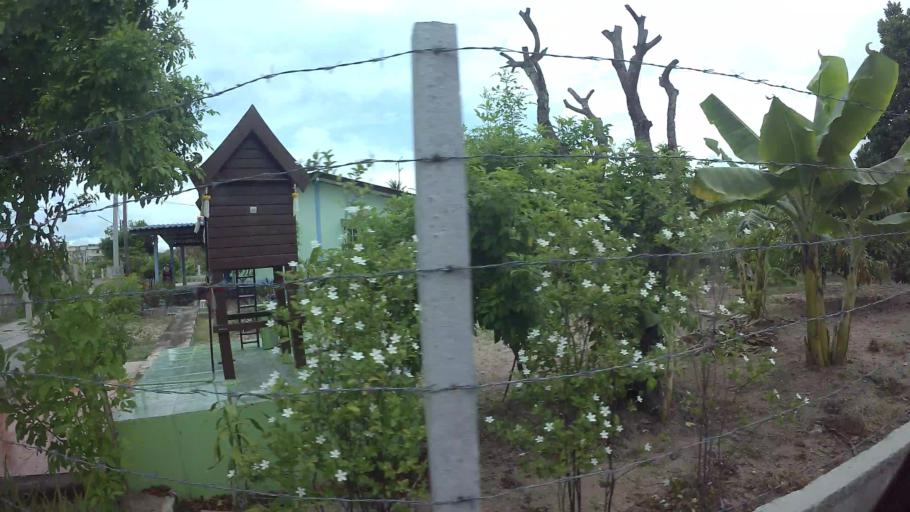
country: TH
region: Chon Buri
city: Si Racha
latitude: 13.1586
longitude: 100.9751
